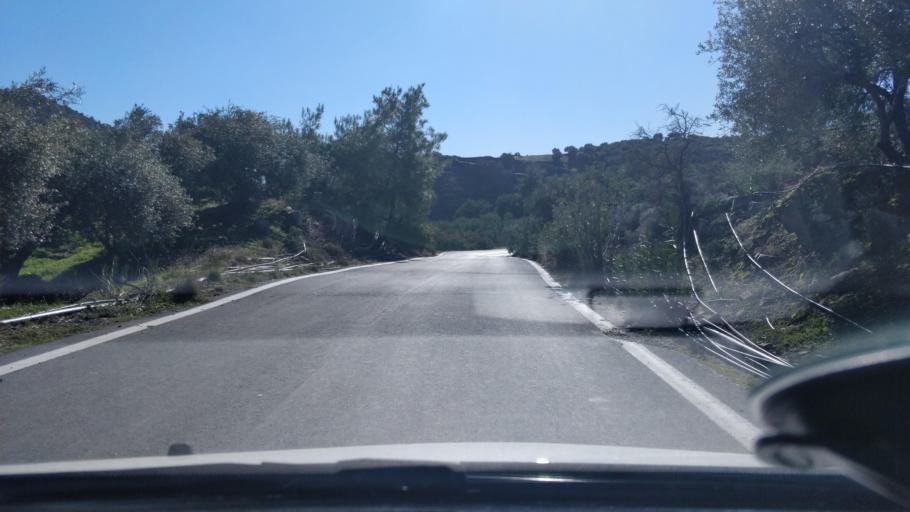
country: GR
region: Crete
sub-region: Nomos Irakleiou
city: Kastelli
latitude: 35.0192
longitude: 25.4491
